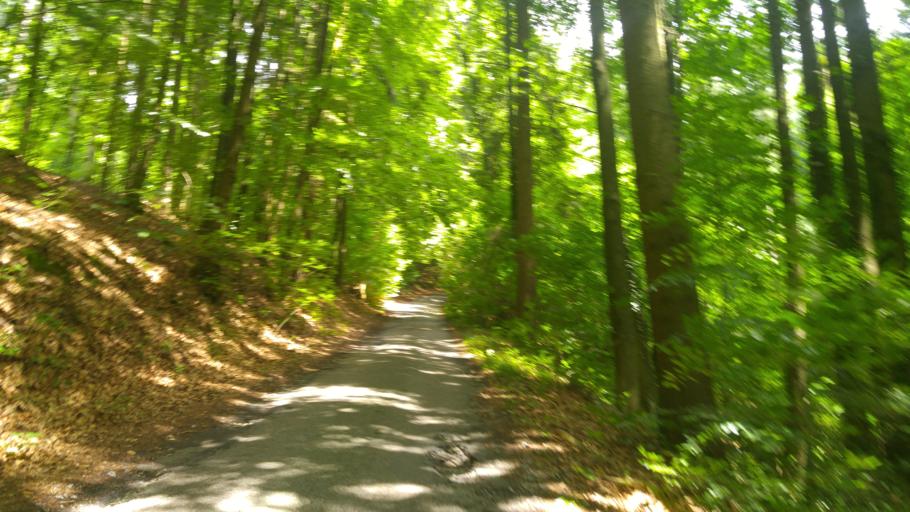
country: DE
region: Baden-Wuerttemberg
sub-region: Regierungsbezirk Stuttgart
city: Wustenrot
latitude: 49.0821
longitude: 9.4513
